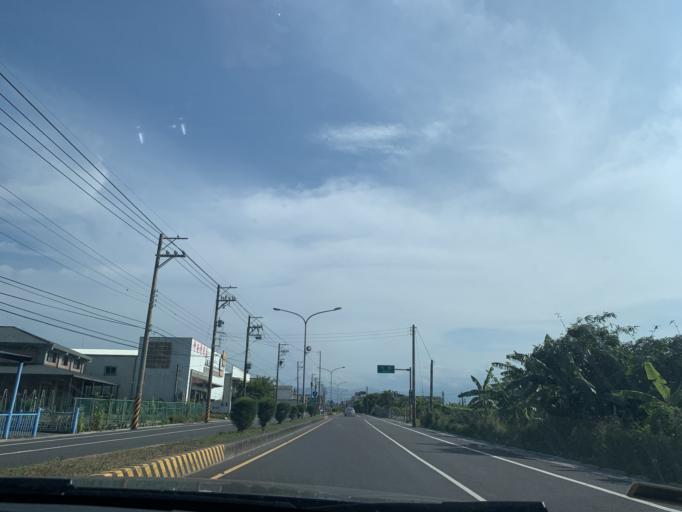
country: TW
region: Taiwan
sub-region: Yilan
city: Yilan
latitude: 24.8307
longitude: 121.8222
